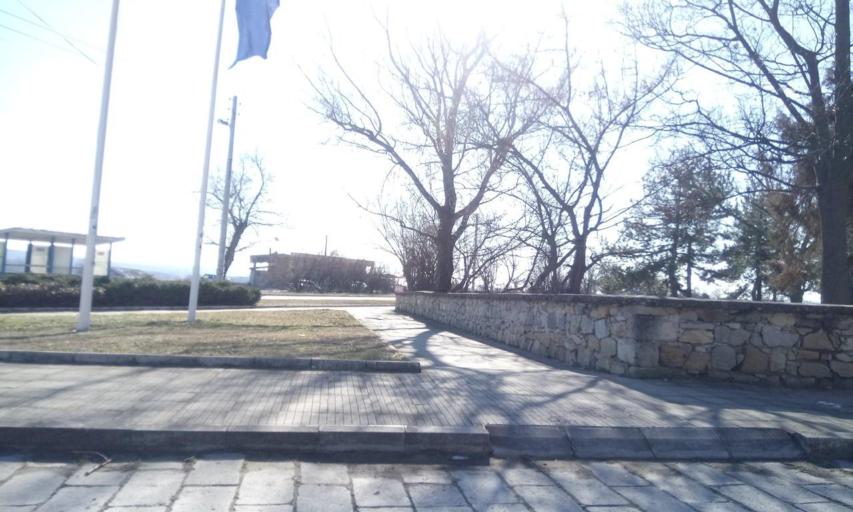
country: BG
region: Plovdiv
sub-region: Obshtina Khisarya
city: Khisarya
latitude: 42.5151
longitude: 24.7186
